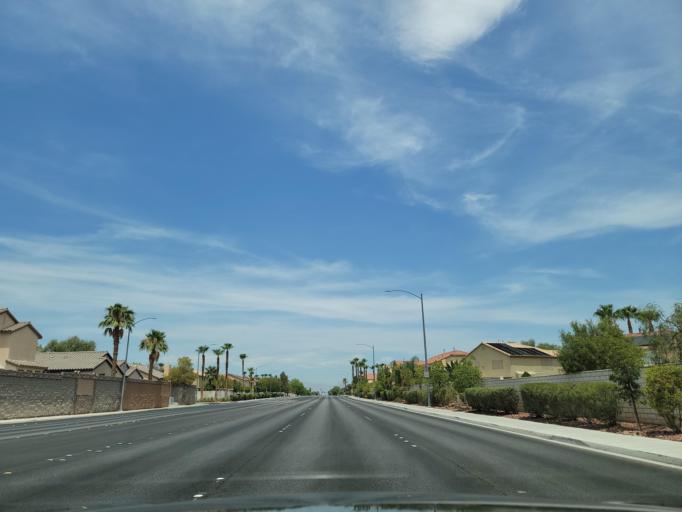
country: US
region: Nevada
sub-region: Clark County
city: Paradise
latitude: 36.0231
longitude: -115.1545
